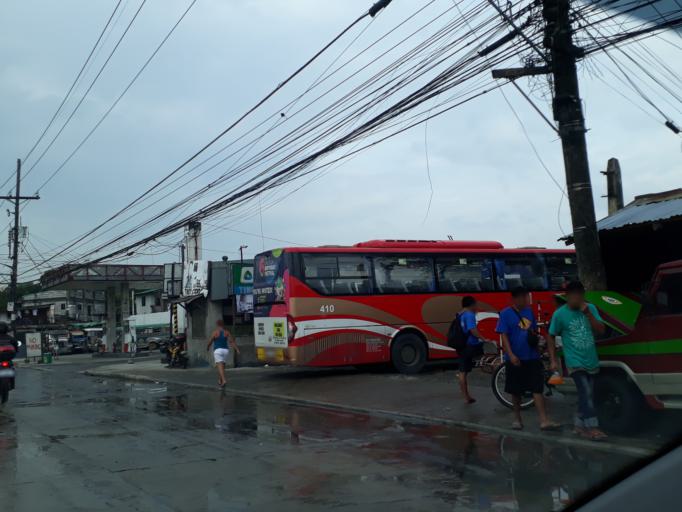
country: PH
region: Central Luzon
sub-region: Province of Bulacan
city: Meycauayan
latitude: 14.7206
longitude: 120.9584
